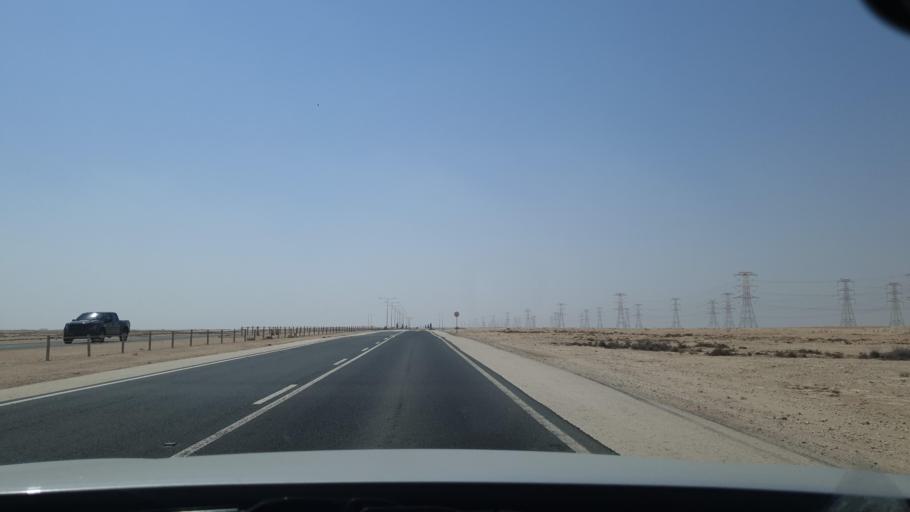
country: QA
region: Al Khawr
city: Al Khawr
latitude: 25.7371
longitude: 51.4596
